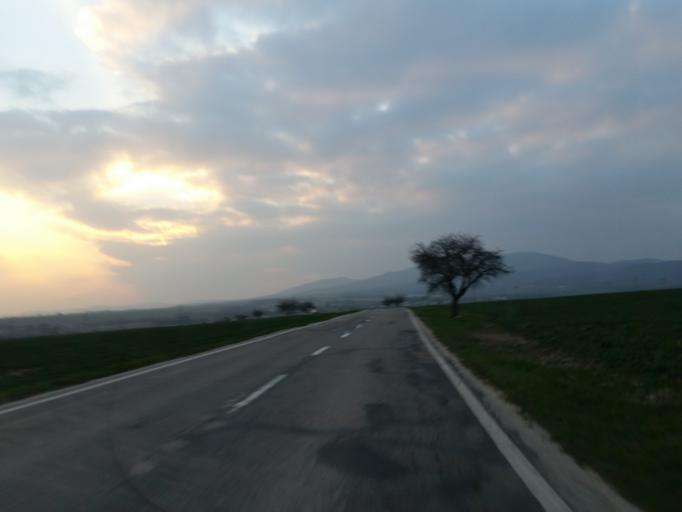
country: SK
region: Nitriansky
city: Banovce nad Bebravou
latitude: 48.5686
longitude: 18.0830
